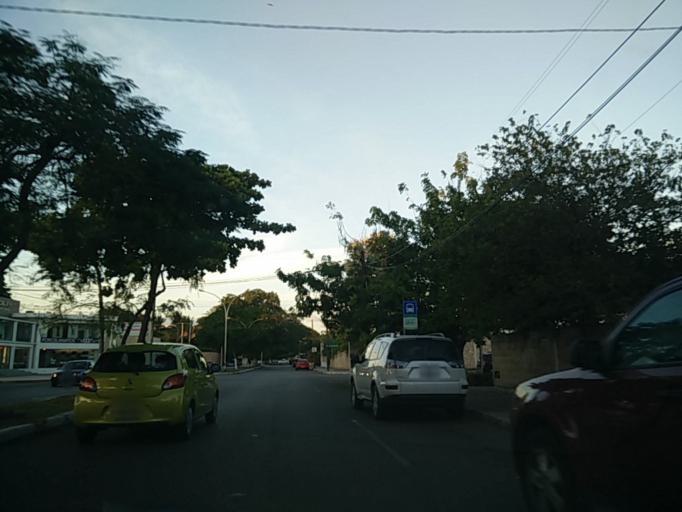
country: MX
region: Yucatan
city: Merida
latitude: 20.9985
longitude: -89.6113
